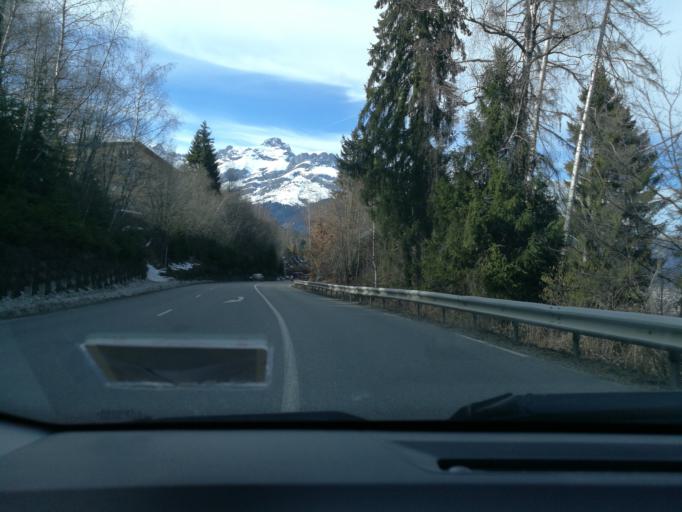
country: FR
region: Rhone-Alpes
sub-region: Departement de la Haute-Savoie
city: Domancy
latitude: 45.9008
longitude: 6.6496
